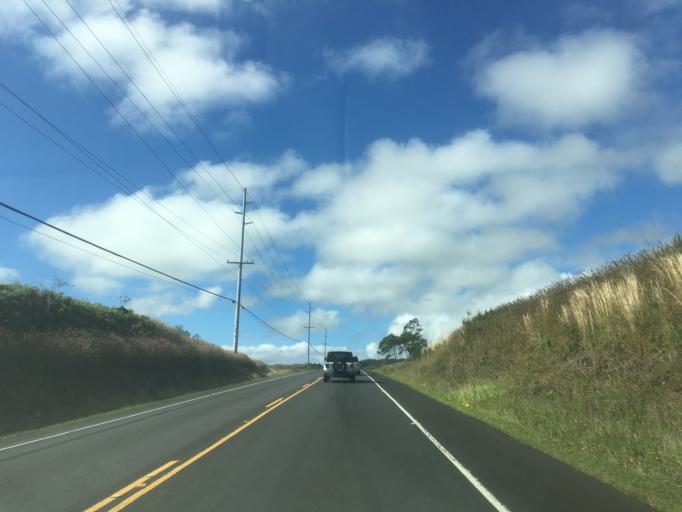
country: US
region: Hawaii
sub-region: Hawaii County
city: Waimea
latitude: 20.0477
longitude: -155.5792
